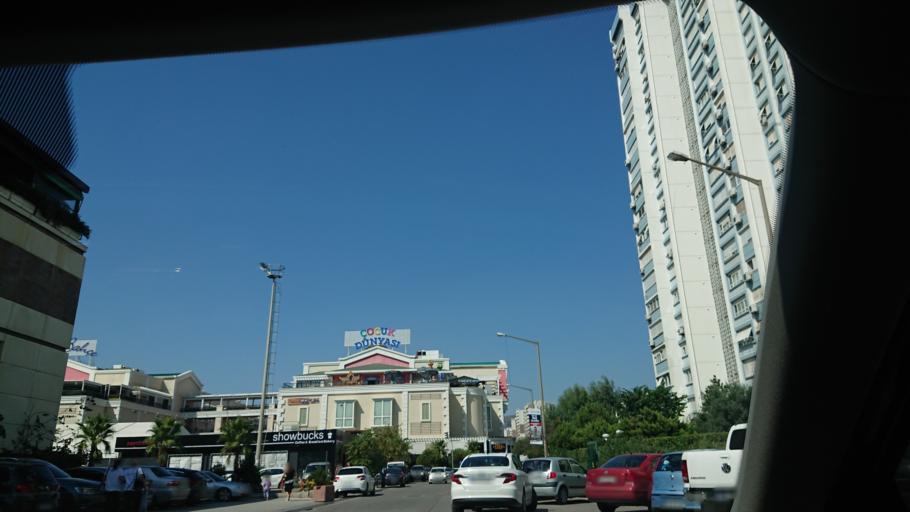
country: TR
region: Izmir
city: Karsiyaka
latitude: 38.4713
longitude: 27.0755
